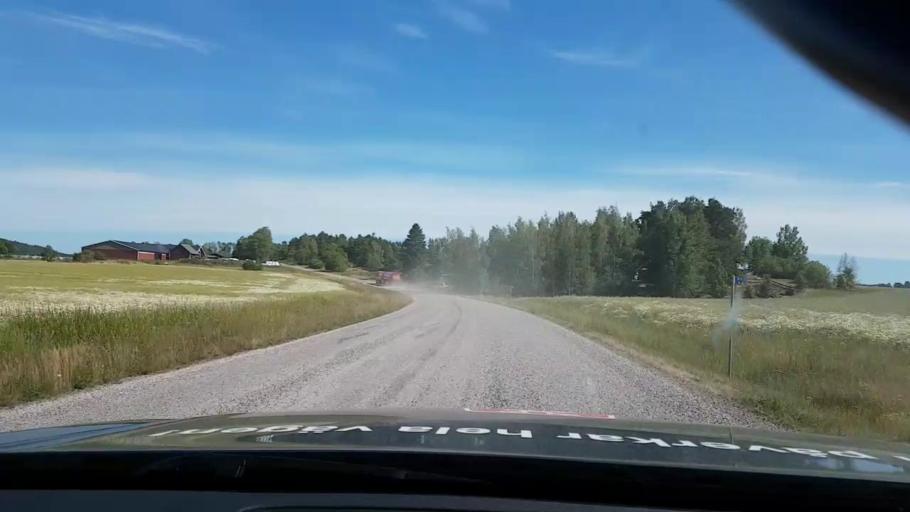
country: SE
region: Kalmar
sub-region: Vasterviks Kommun
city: Forserum
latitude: 57.9410
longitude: 16.4534
